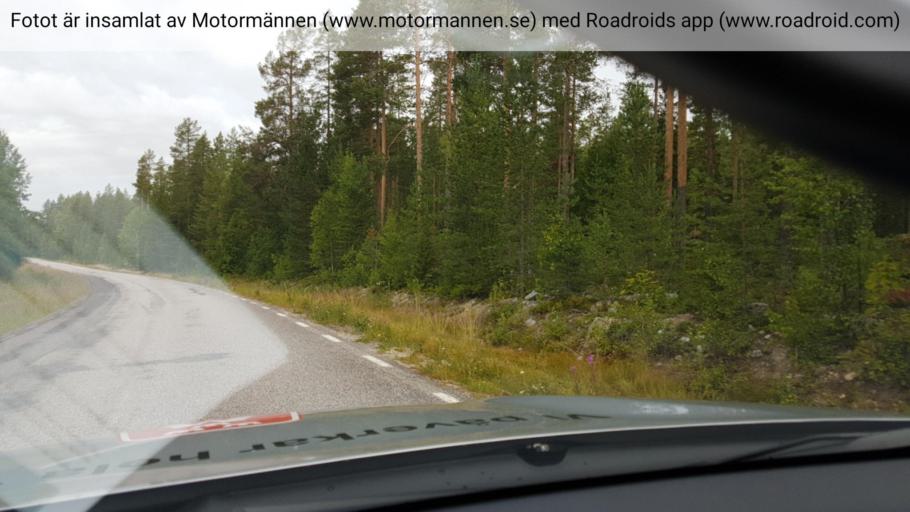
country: SE
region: Norrbotten
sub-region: Bodens Kommun
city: Saevast
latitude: 65.6705
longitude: 21.7073
